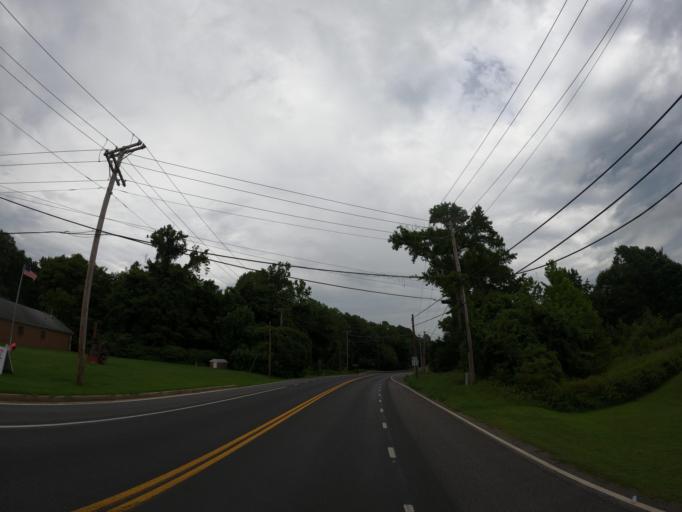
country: US
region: Maryland
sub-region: Saint Mary's County
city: Lexington Park
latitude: 38.1939
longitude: -76.5139
